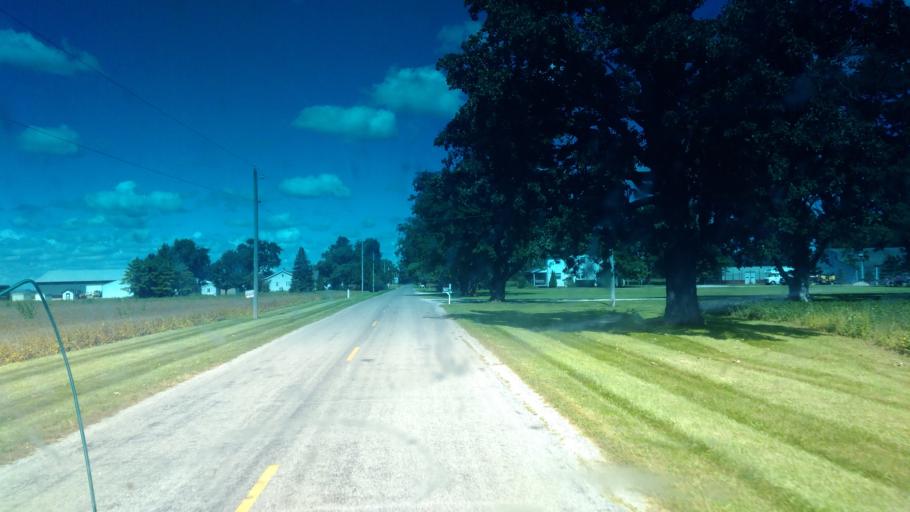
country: US
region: Ohio
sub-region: Madison County
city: Plain City
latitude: 40.0650
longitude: -83.3434
